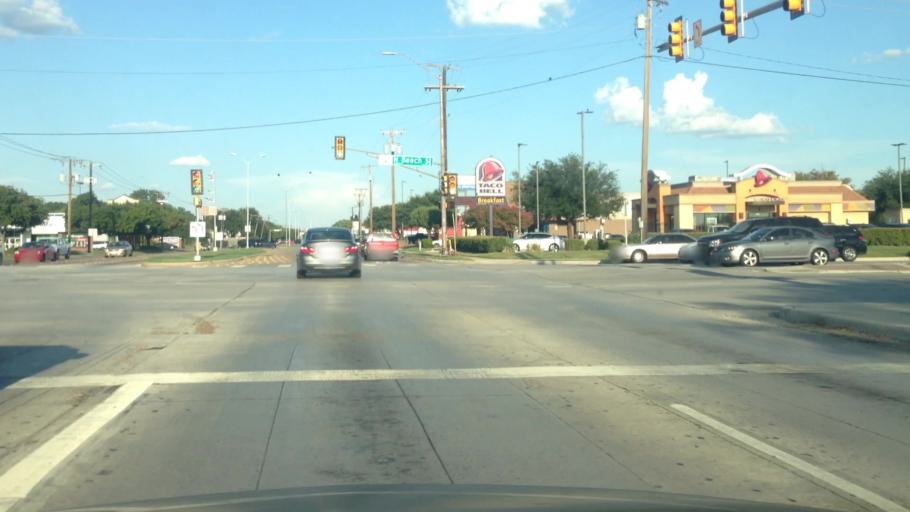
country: US
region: Texas
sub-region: Tarrant County
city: Watauga
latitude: 32.8610
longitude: -97.2904
